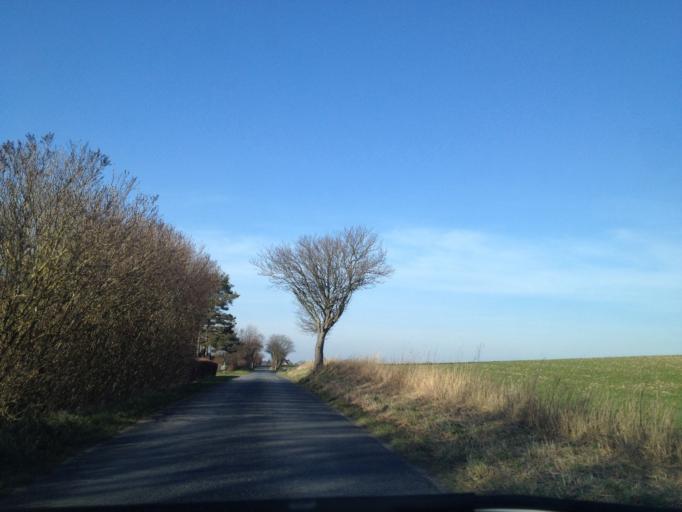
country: DK
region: South Denmark
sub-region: Kerteminde Kommune
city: Munkebo
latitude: 55.5679
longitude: 10.6113
